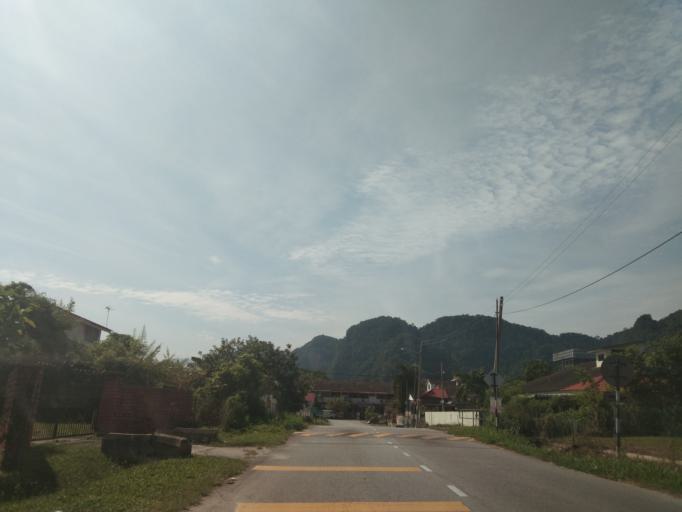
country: MY
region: Perak
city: Ipoh
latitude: 4.5689
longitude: 101.1279
